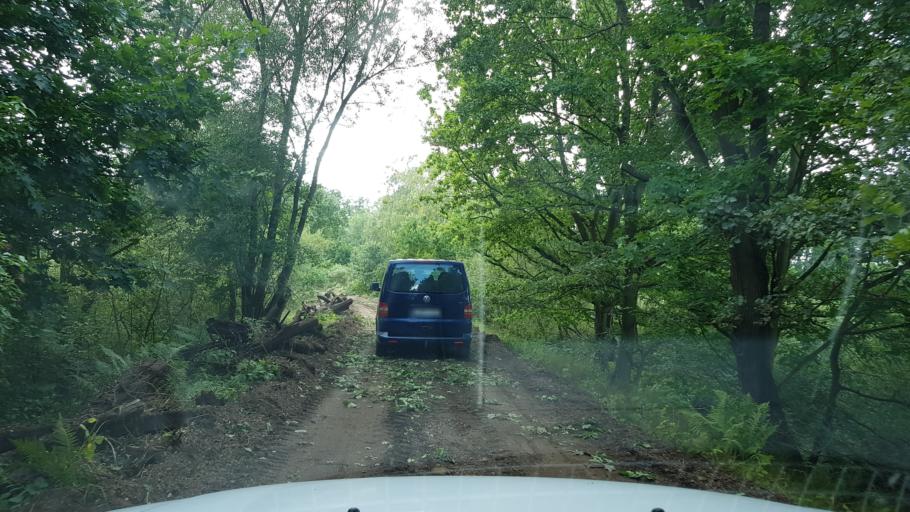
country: PL
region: West Pomeranian Voivodeship
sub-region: Powiat choszczenski
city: Pelczyce
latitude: 53.0868
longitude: 15.3026
